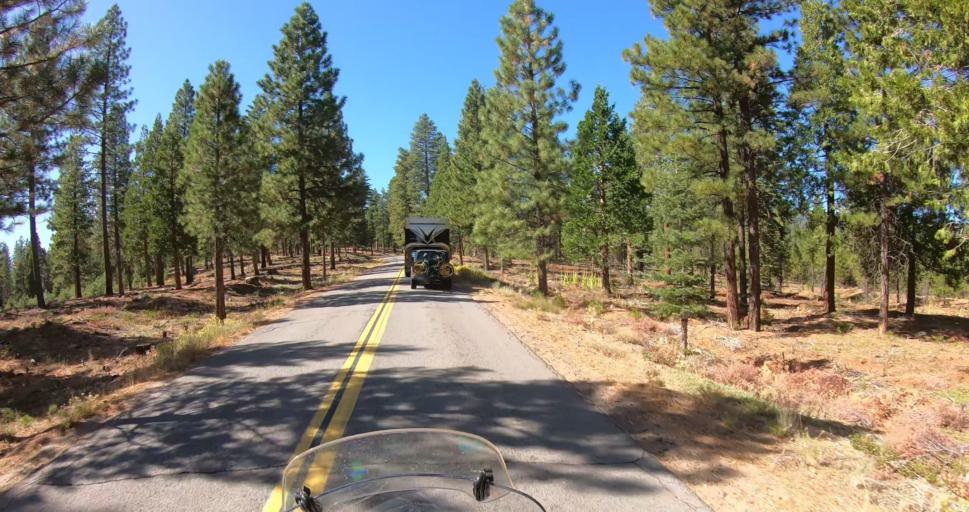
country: US
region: California
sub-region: Lassen County
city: Susanville
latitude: 40.4446
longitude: -120.7536
